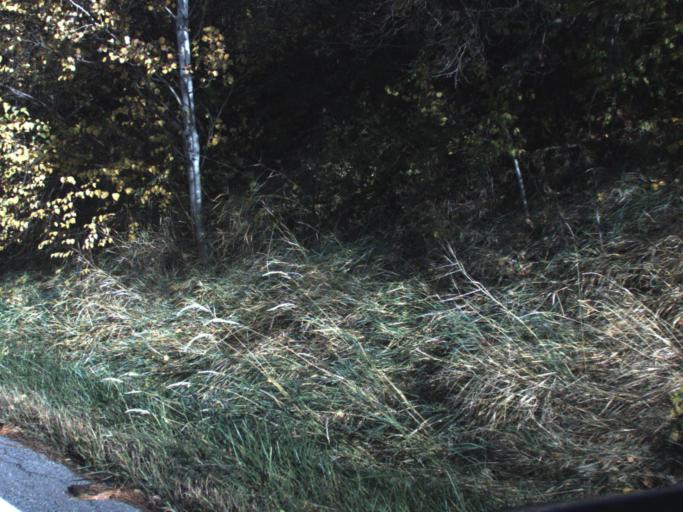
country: US
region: Washington
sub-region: Stevens County
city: Kettle Falls
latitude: 48.5622
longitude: -118.1185
